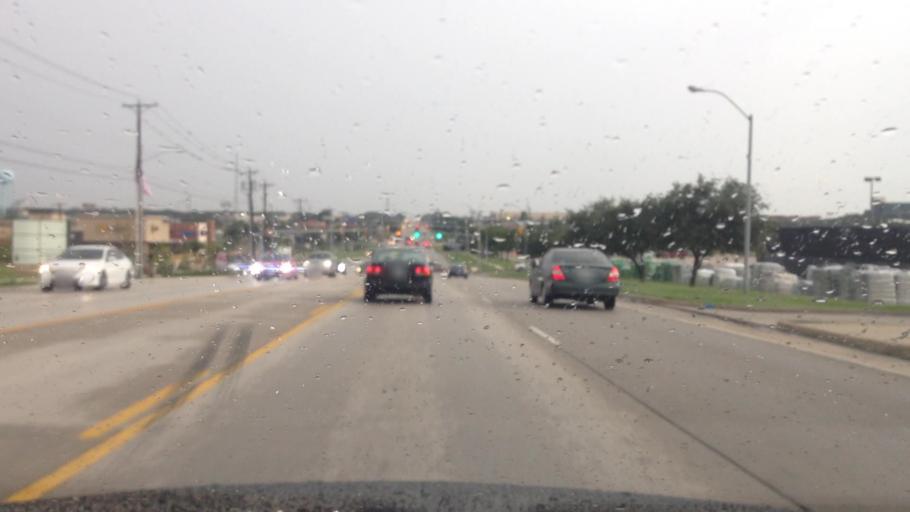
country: US
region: Texas
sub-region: Tarrant County
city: Colleyville
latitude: 32.8586
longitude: -97.1827
